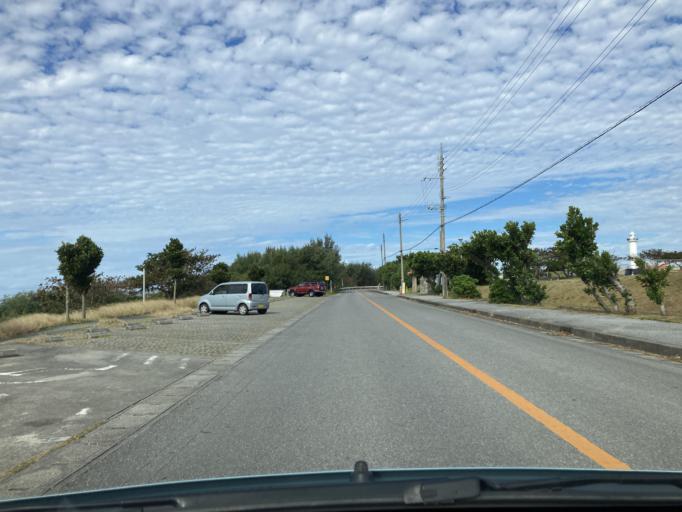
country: JP
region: Okinawa
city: Ishikawa
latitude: 26.4379
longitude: 127.7148
